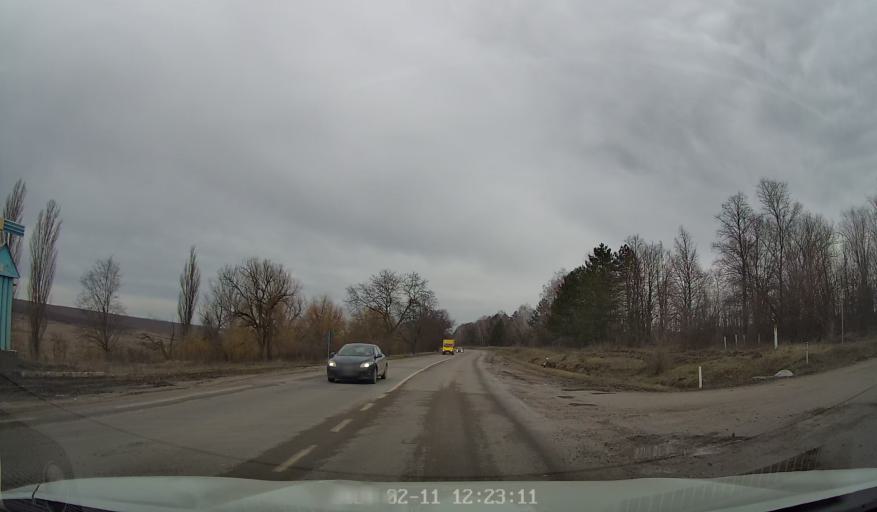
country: MD
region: Raionul Edinet
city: Edinet
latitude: 48.1337
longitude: 27.3602
